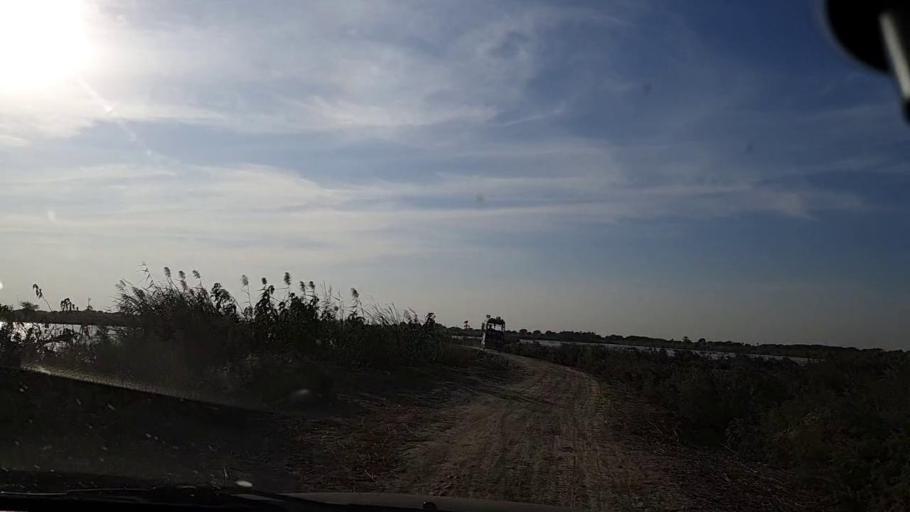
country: PK
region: Sindh
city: Mirpur Batoro
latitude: 24.6548
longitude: 68.2942
